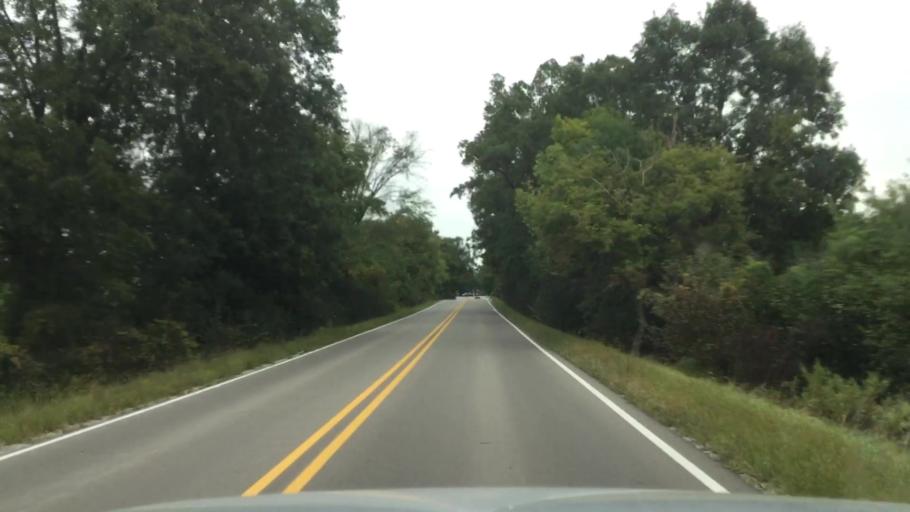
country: US
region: Michigan
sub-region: Washtenaw County
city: Ypsilanti
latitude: 42.1990
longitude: -83.6265
